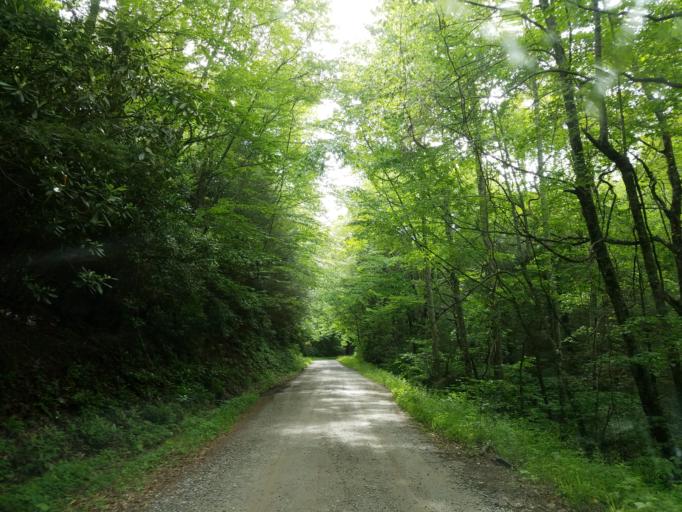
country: US
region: Georgia
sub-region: Union County
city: Blairsville
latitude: 34.7381
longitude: -83.9929
